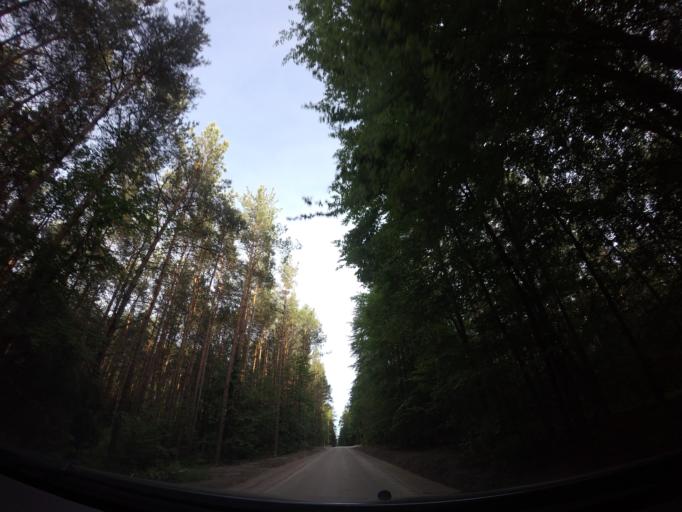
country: PL
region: West Pomeranian Voivodeship
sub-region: Powiat choszczenski
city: Bierzwnik
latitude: 53.0205
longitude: 15.6078
